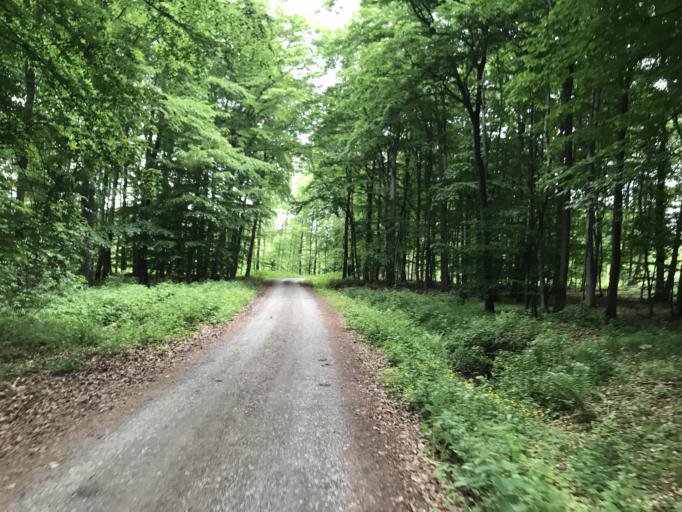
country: DE
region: Hesse
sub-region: Regierungsbezirk Kassel
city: Martinhagen
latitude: 51.2917
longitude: 9.2672
